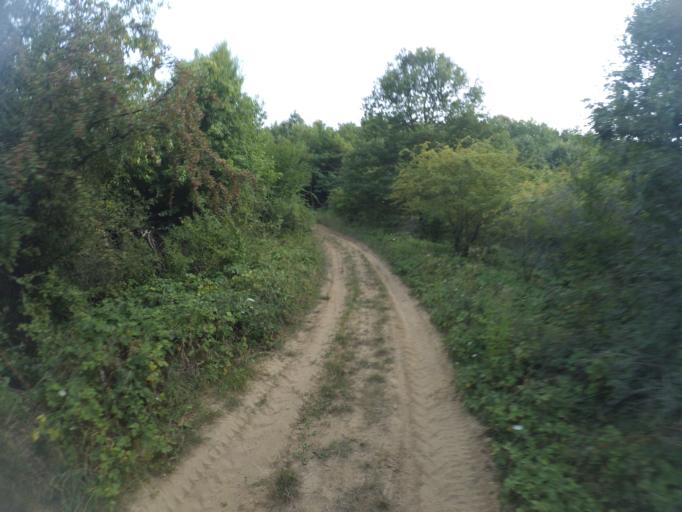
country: HU
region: Pest
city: Pilisszanto
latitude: 47.6702
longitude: 18.8705
